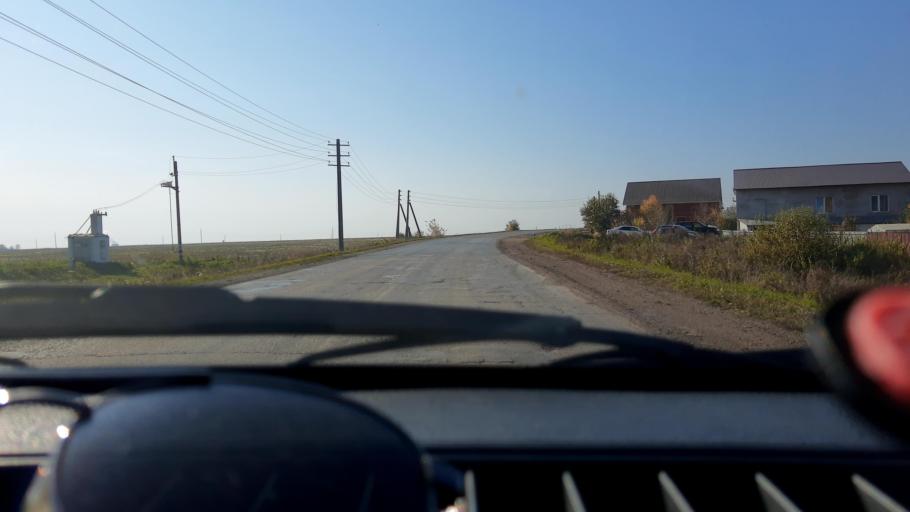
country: RU
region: Bashkortostan
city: Mikhaylovka
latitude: 54.8425
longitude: 55.8409
